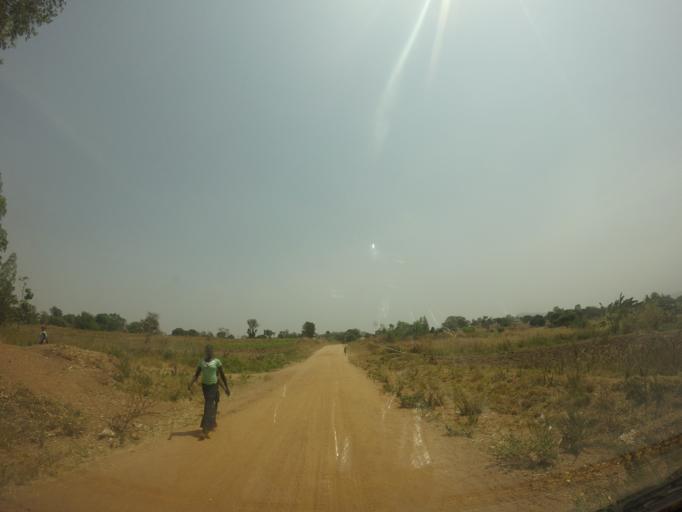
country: UG
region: Northern Region
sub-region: Arua District
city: Arua
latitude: 2.9153
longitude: 31.0226
